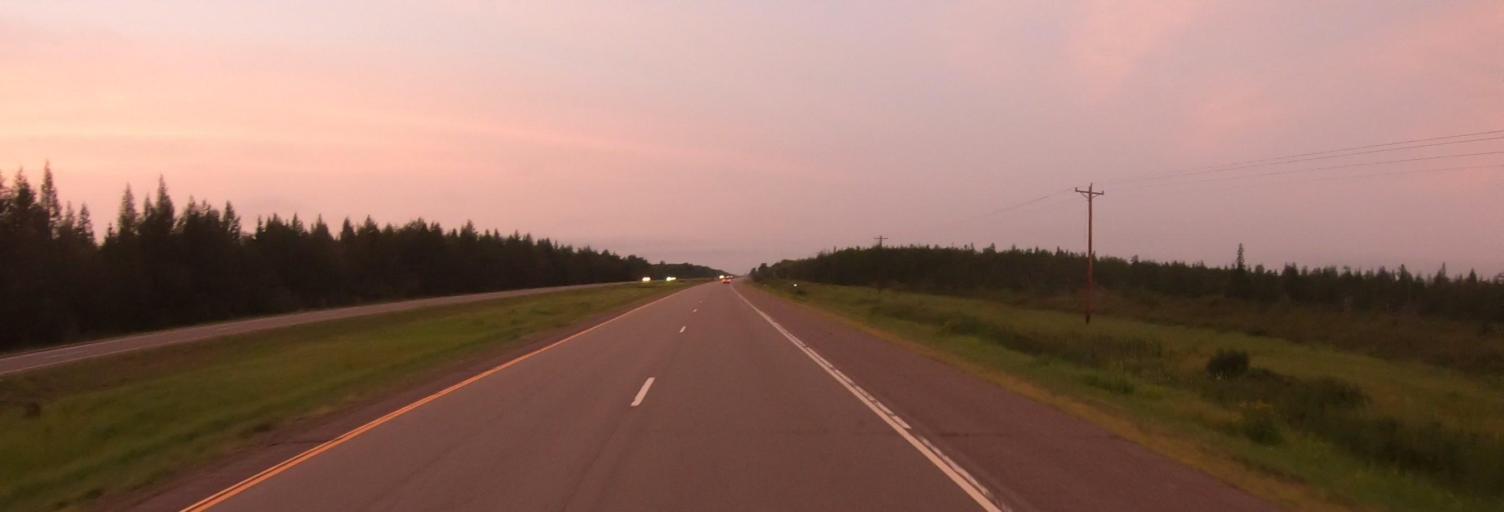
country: US
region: Minnesota
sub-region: Carlton County
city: Cloquet
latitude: 47.0740
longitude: -92.4715
